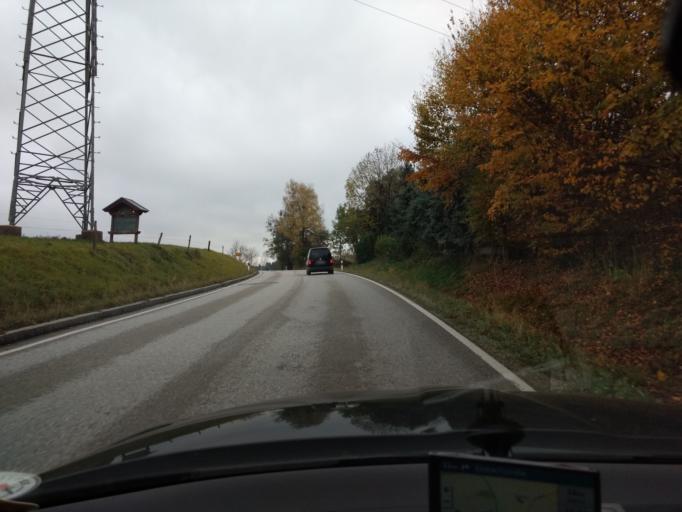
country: DE
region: Bavaria
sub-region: Upper Bavaria
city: Konigsdorf
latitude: 47.8153
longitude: 11.4836
